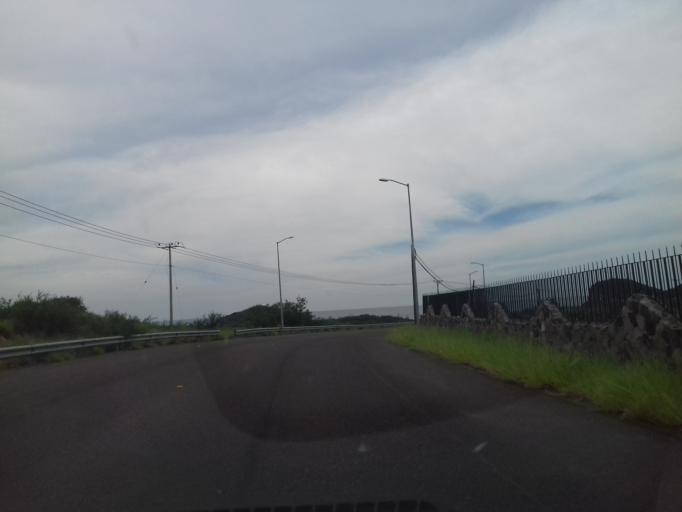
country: MX
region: Sonora
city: Heroica Guaymas
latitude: 27.9441
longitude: -111.0877
